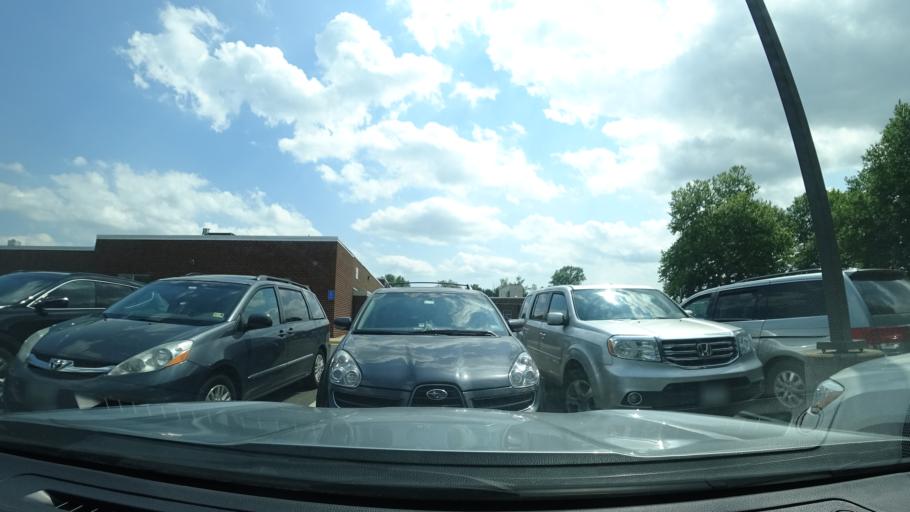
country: US
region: Virginia
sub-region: Fairfax County
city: Floris
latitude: 38.9363
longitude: -77.4145
